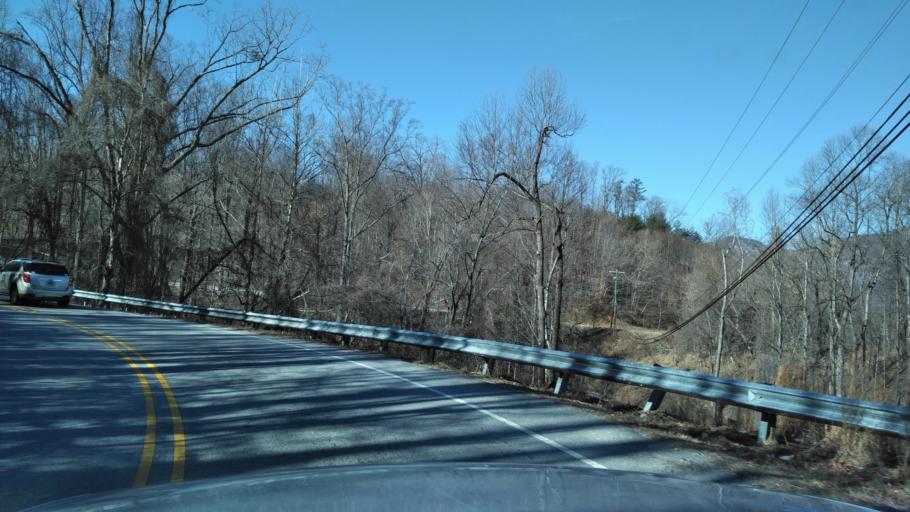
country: US
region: North Carolina
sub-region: Rutherford County
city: Lake Lure
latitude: 35.4268
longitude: -82.2032
